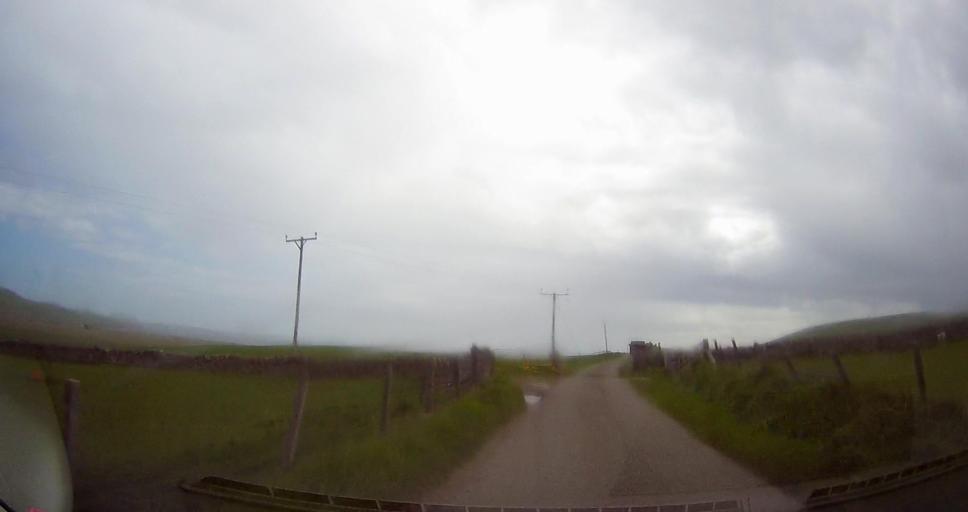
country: GB
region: Scotland
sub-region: Shetland Islands
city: Sandwick
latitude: 59.9069
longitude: -1.3347
